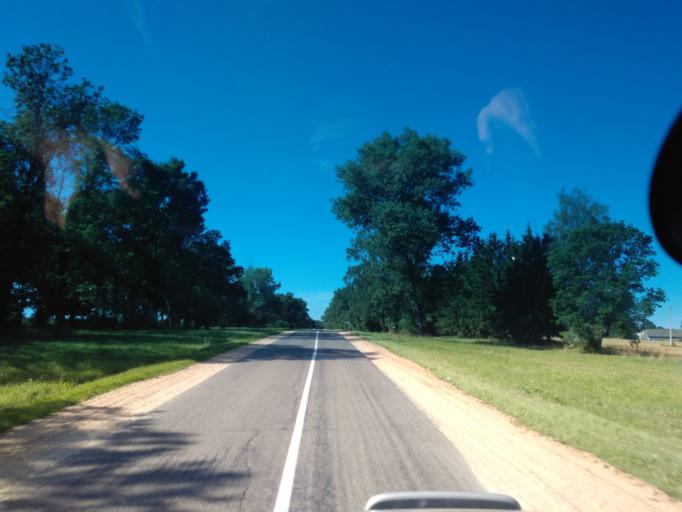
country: BY
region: Minsk
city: Stan'kava
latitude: 53.6348
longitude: 27.2795
